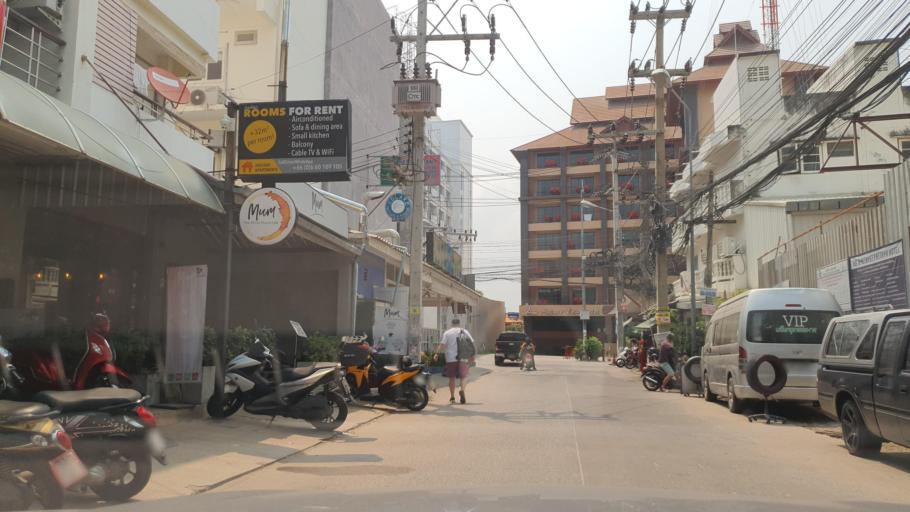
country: TH
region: Chon Buri
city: Phatthaya
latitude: 12.9277
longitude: 100.8833
